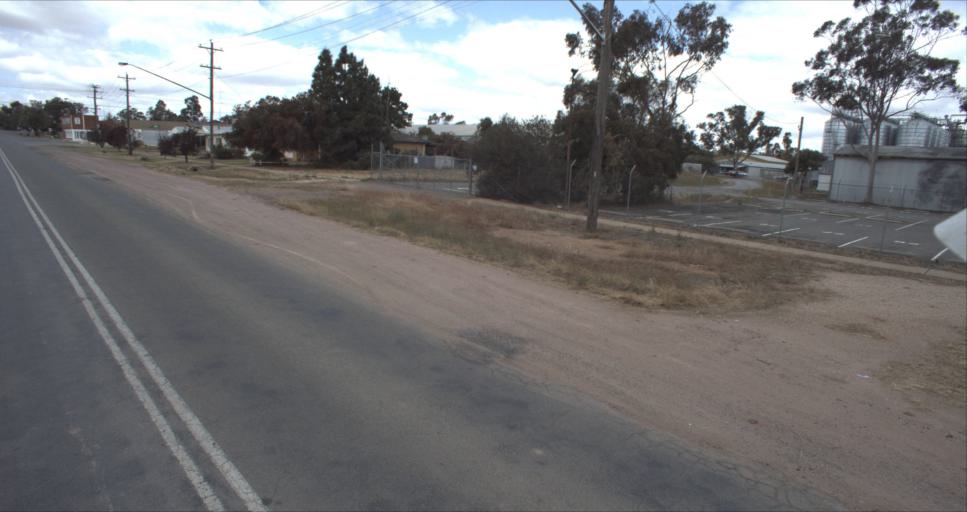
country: AU
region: New South Wales
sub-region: Leeton
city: Leeton
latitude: -34.5550
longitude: 146.3969
